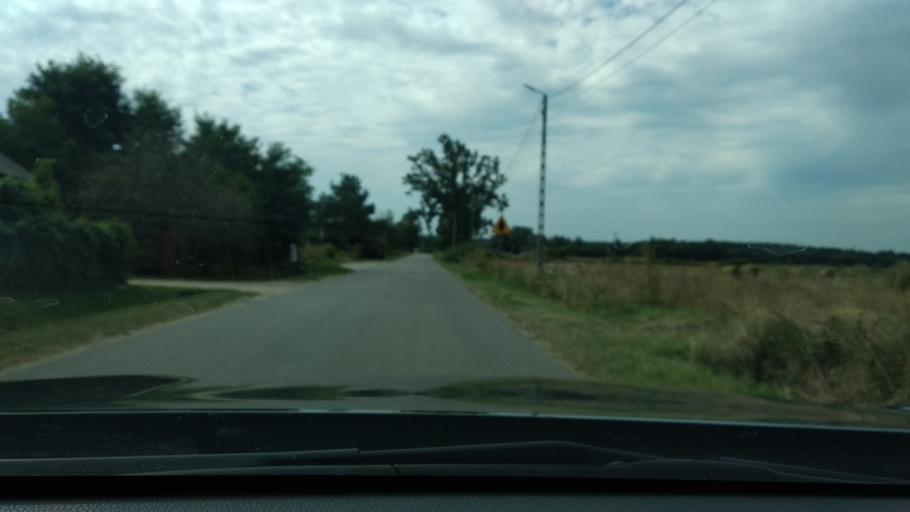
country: PL
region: Masovian Voivodeship
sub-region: Powiat pultuski
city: Zatory
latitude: 52.6524
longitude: 21.1862
